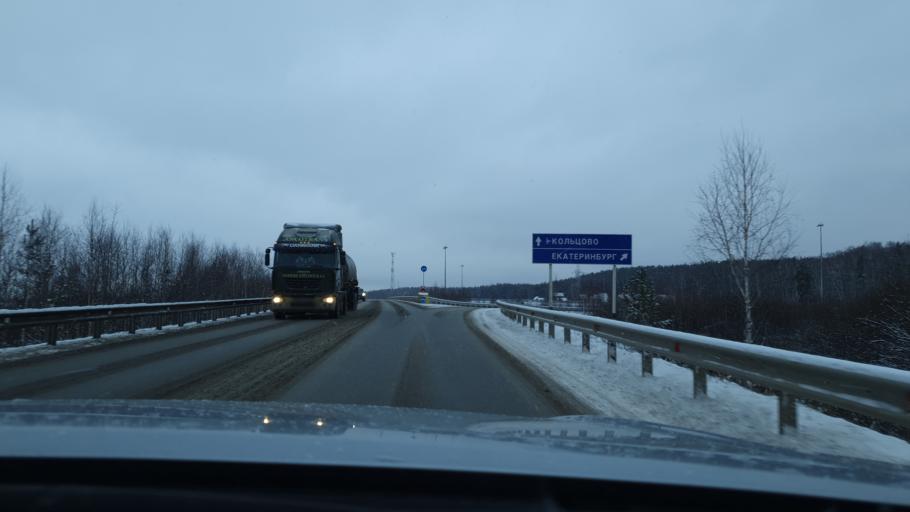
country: RU
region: Sverdlovsk
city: Istok
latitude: 56.7718
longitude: 60.7375
